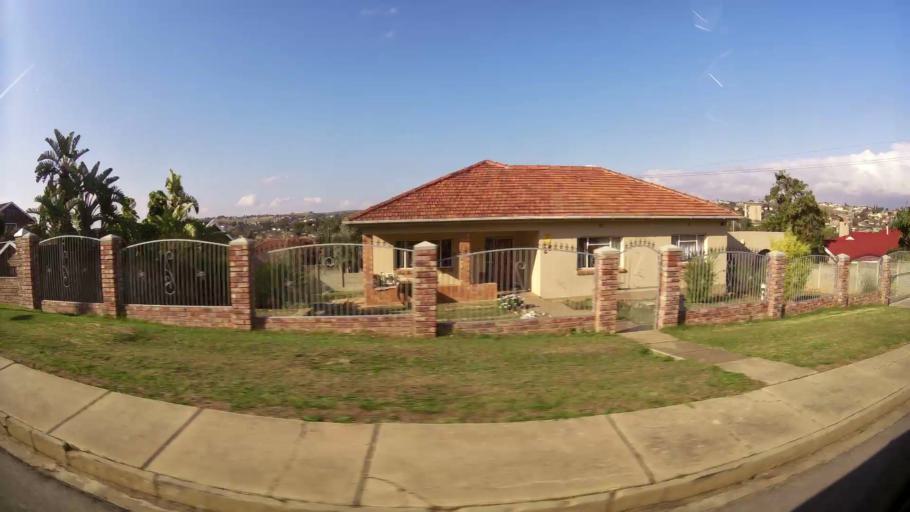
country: ZA
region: Eastern Cape
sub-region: Nelson Mandela Bay Metropolitan Municipality
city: Uitenhage
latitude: -33.7653
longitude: 25.4085
